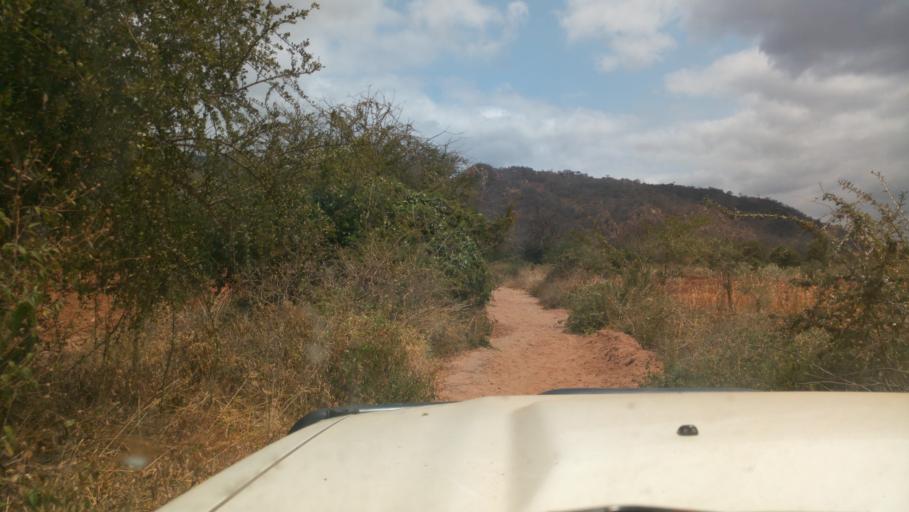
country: KE
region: Kitui
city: Kitui
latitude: -1.8710
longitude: 38.3636
